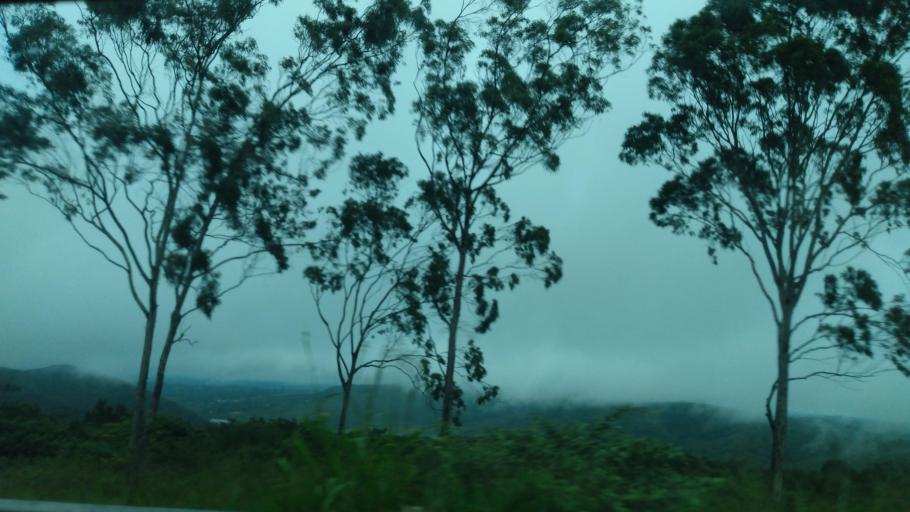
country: BR
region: Pernambuco
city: Garanhuns
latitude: -8.8748
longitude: -36.5311
